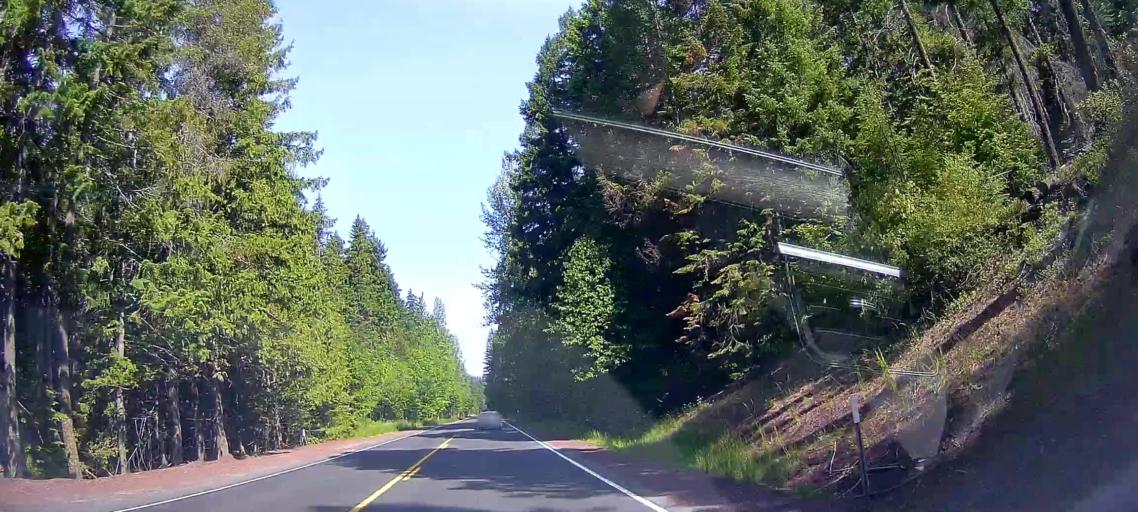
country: US
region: Oregon
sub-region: Clackamas County
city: Mount Hood Village
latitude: 45.1173
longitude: -121.5793
